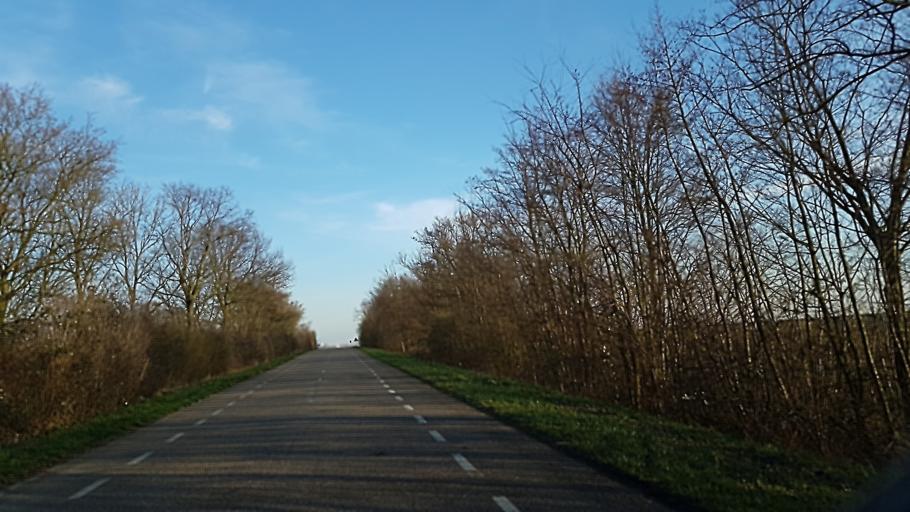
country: NL
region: North Brabant
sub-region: Gemeente Woensdrecht
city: Woensdrecht
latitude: 51.4056
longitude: 4.2128
